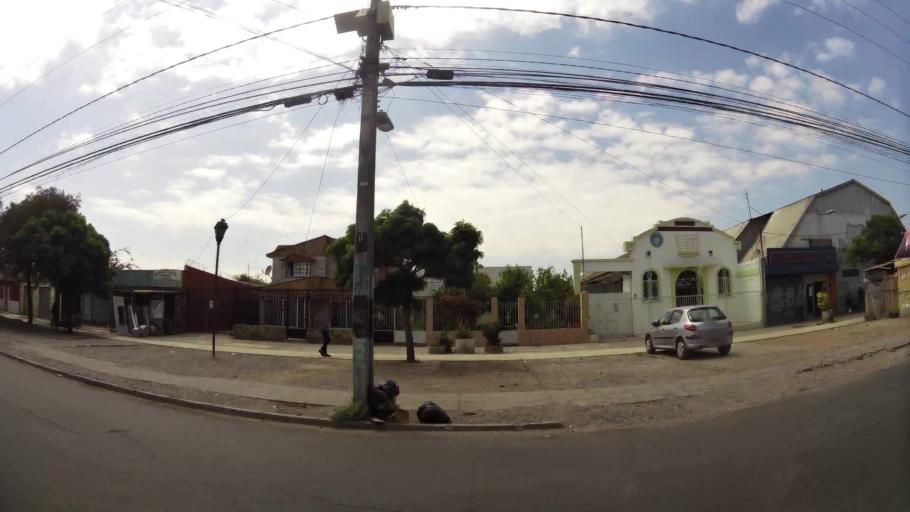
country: CL
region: Santiago Metropolitan
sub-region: Provincia de Santiago
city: Santiago
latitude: -33.5044
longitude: -70.6912
